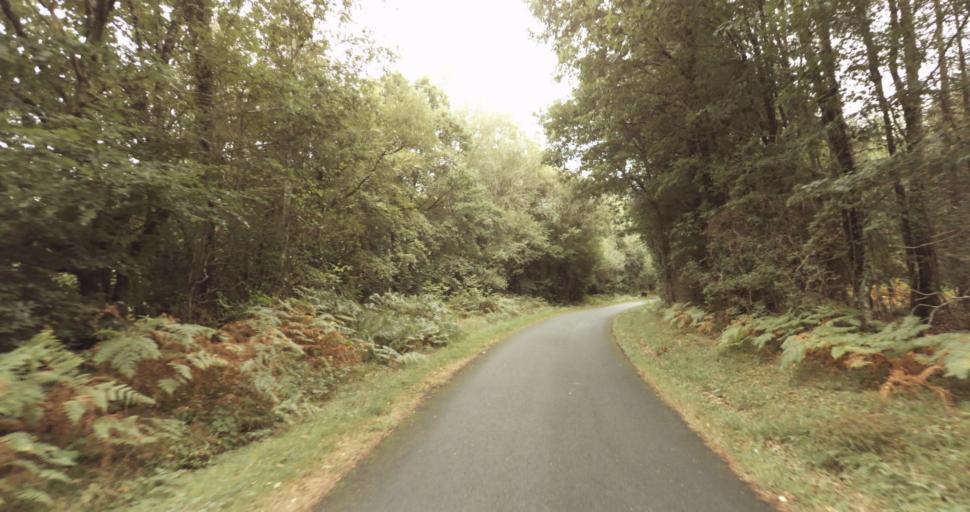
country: FR
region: Lower Normandy
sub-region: Departement de l'Orne
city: Gace
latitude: 48.8403
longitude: 0.3319
